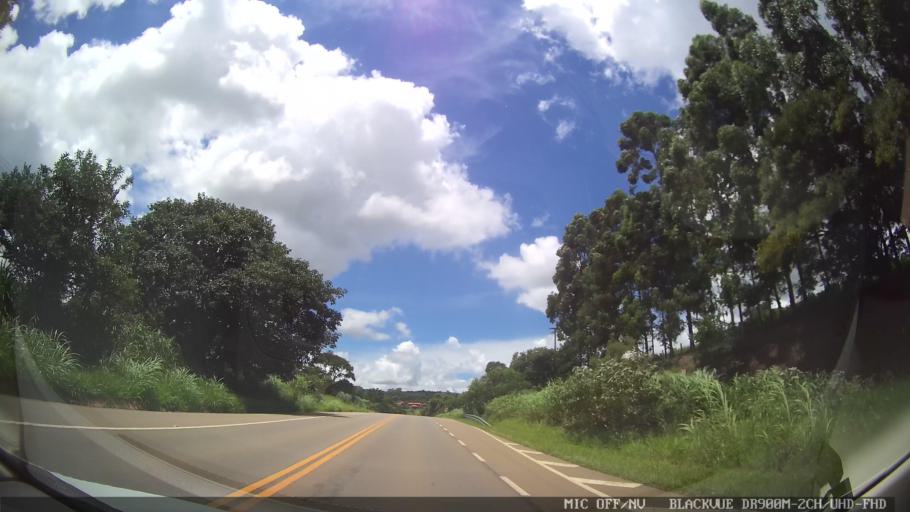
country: BR
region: Sao Paulo
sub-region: Amparo
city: Amparo
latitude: -22.8369
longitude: -46.6669
